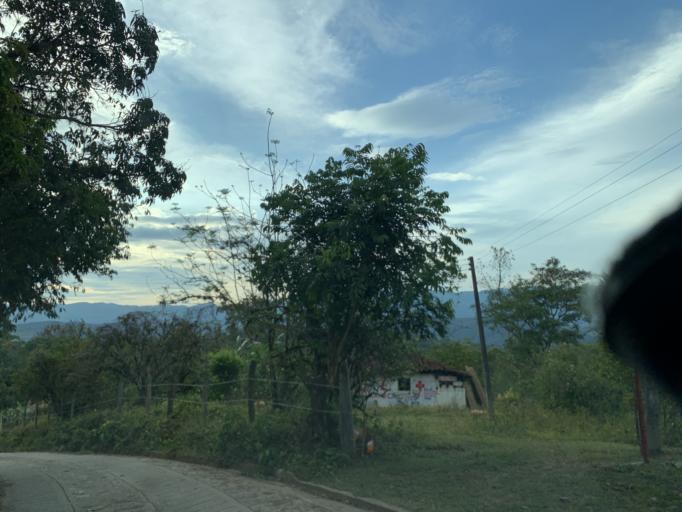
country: CO
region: Boyaca
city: Santana
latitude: 6.0815
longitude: -73.4920
